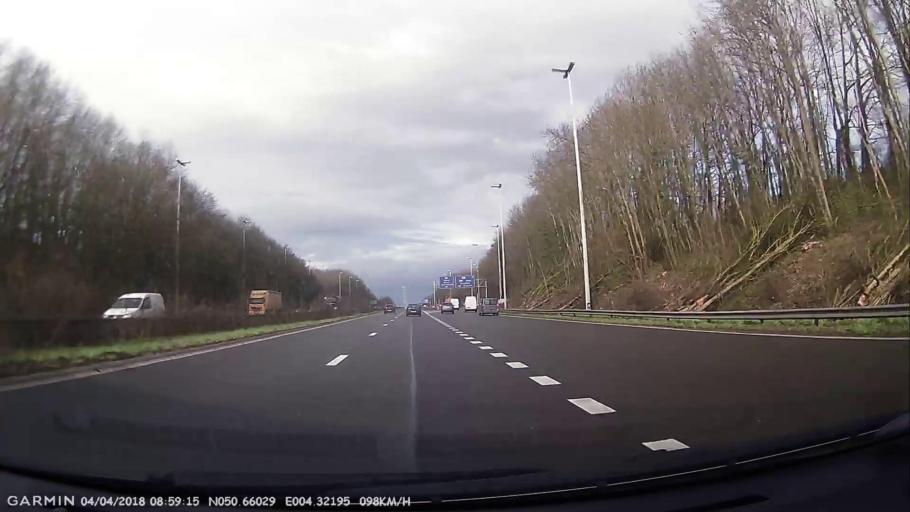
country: BE
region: Wallonia
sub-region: Province du Brabant Wallon
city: Braine-le-Chateau
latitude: 50.6603
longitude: 4.3212
